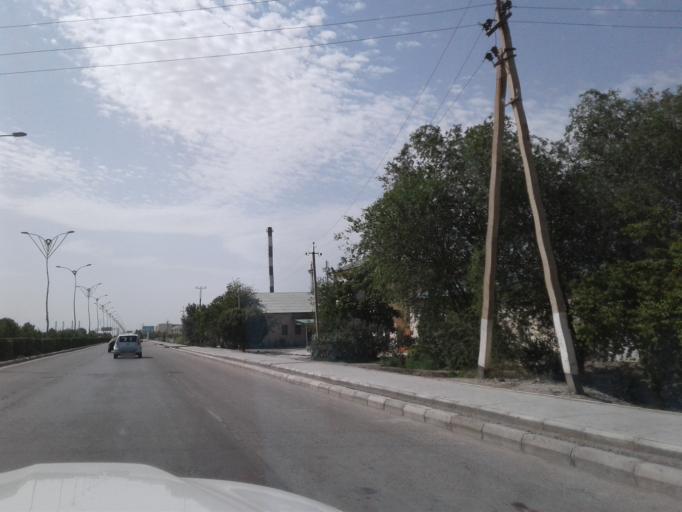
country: TM
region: Dasoguz
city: Dasoguz
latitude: 41.8325
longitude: 59.9380
